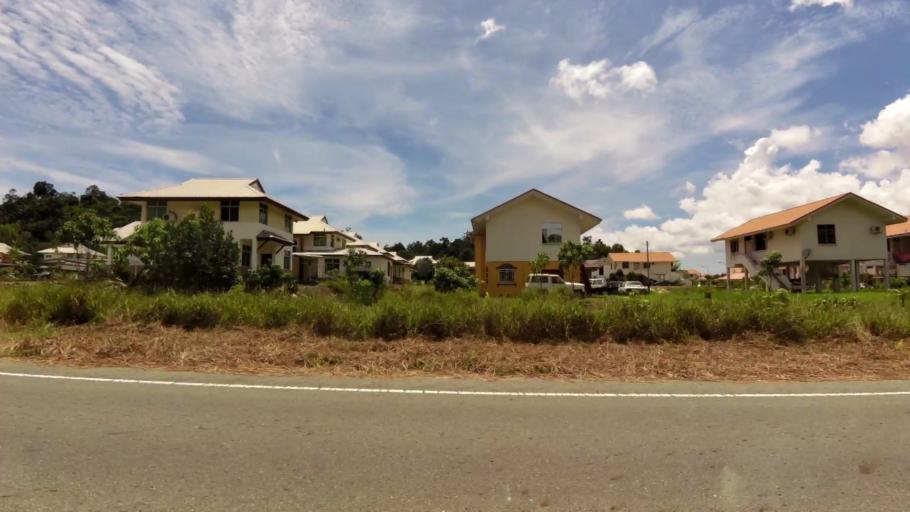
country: BN
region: Brunei and Muara
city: Bandar Seri Begawan
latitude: 4.9642
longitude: 114.9050
